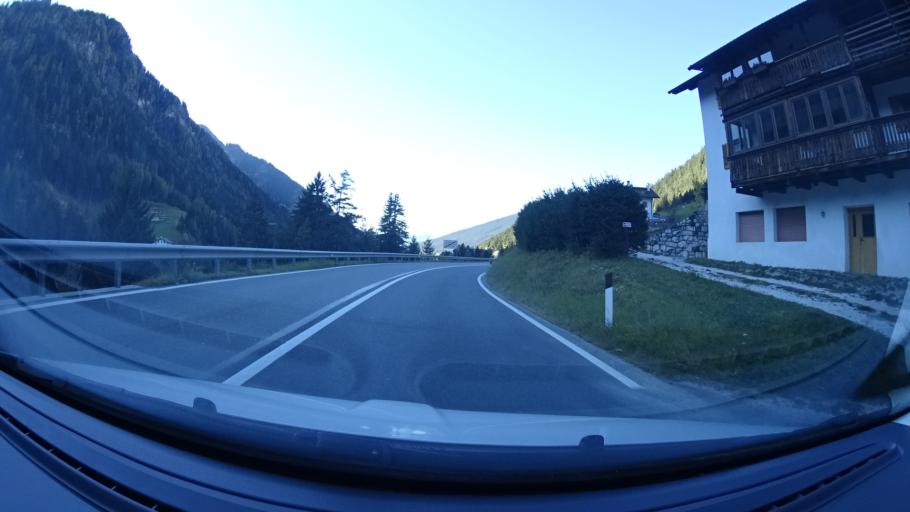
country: IT
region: Trentino-Alto Adige
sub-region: Bolzano
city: Santa Cristina Valgardena
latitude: 46.5615
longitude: 11.7040
